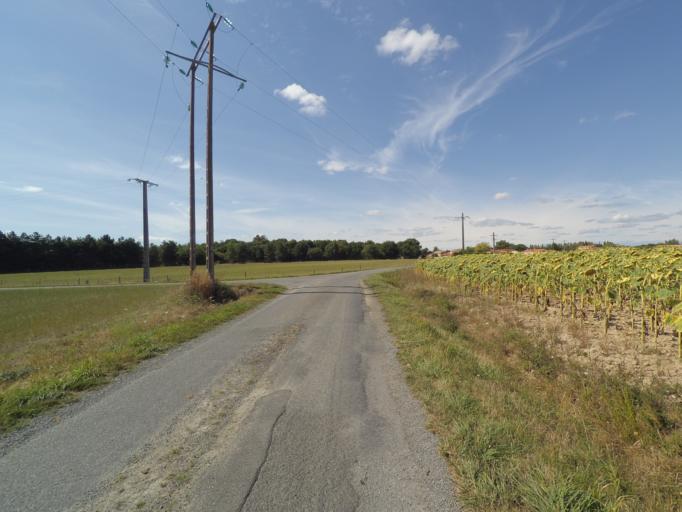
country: FR
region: Pays de la Loire
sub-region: Departement de la Loire-Atlantique
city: Vieillevigne
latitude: 46.9658
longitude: -1.4191
